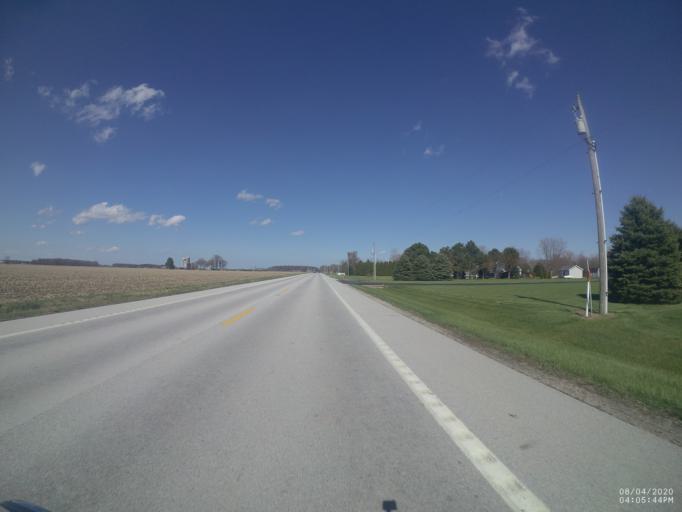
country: US
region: Ohio
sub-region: Sandusky County
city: Ballville
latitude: 41.2644
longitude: -83.2104
